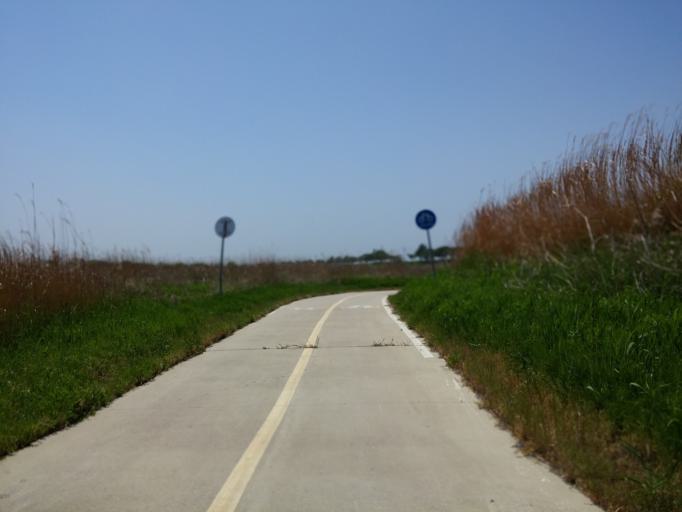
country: KR
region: Chungcheongnam-do
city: Nonsan
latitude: 36.2149
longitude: 127.0913
